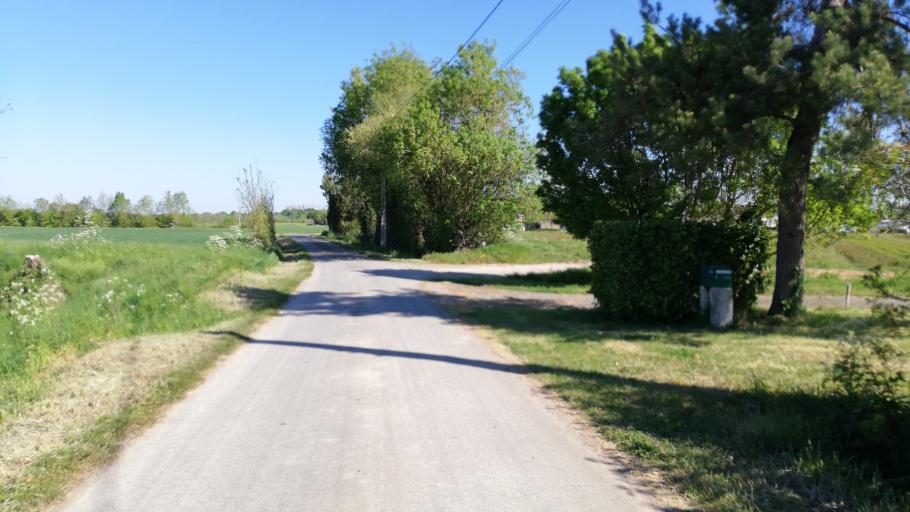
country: FR
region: Pays de la Loire
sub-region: Departement de la Vendee
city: Maillezais
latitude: 46.3281
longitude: -0.7499
